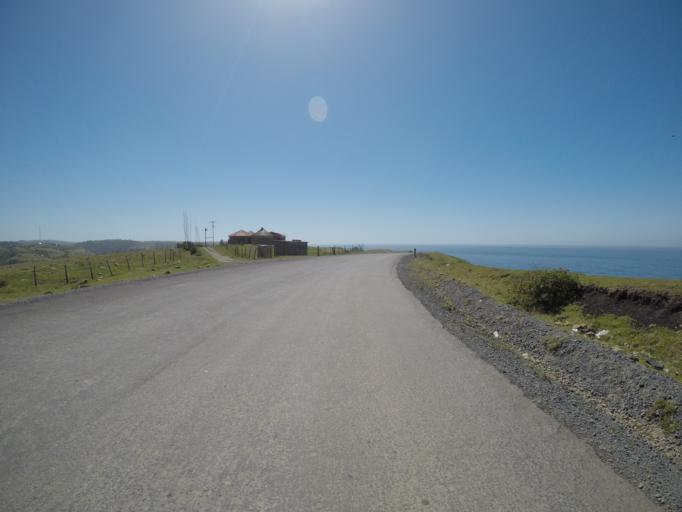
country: ZA
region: Eastern Cape
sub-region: OR Tambo District Municipality
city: Libode
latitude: -31.9916
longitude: 29.1419
